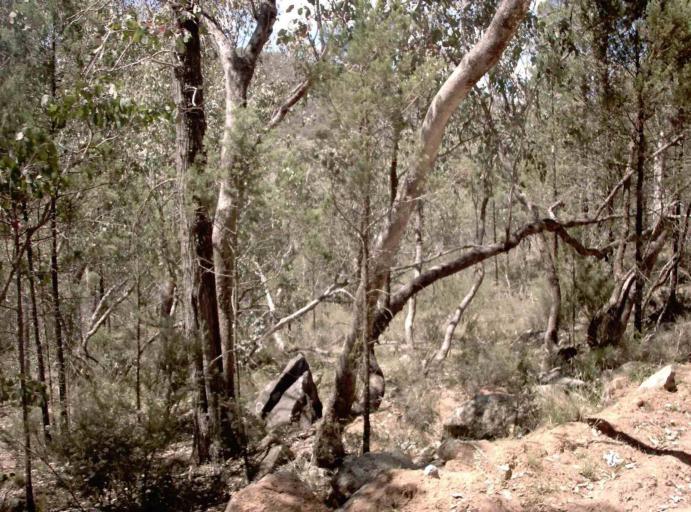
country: AU
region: New South Wales
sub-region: Snowy River
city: Jindabyne
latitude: -37.0895
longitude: 148.4339
